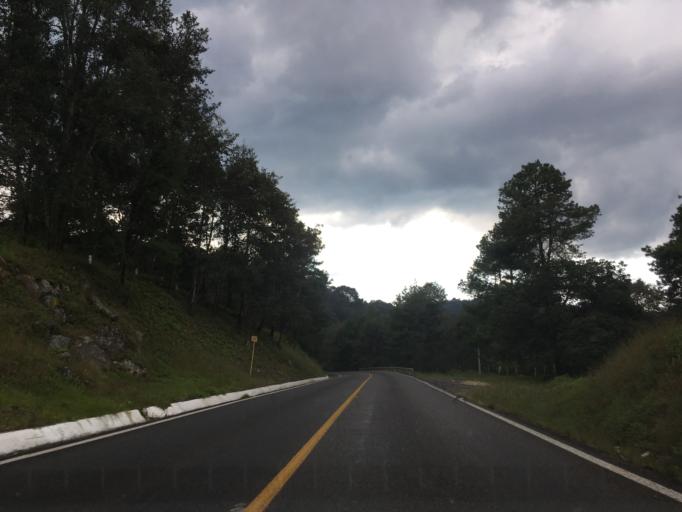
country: MX
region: Michoacan
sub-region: Patzcuaro
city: Santa Maria Huiramangaro (San Juan Tumbio)
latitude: 19.4919
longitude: -101.7229
